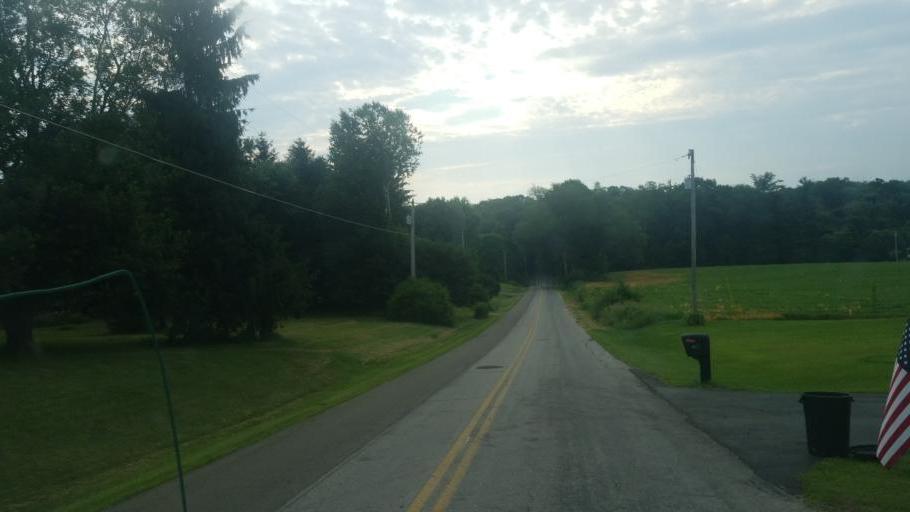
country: US
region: Ohio
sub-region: Wayne County
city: Wooster
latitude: 40.7846
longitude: -81.9932
